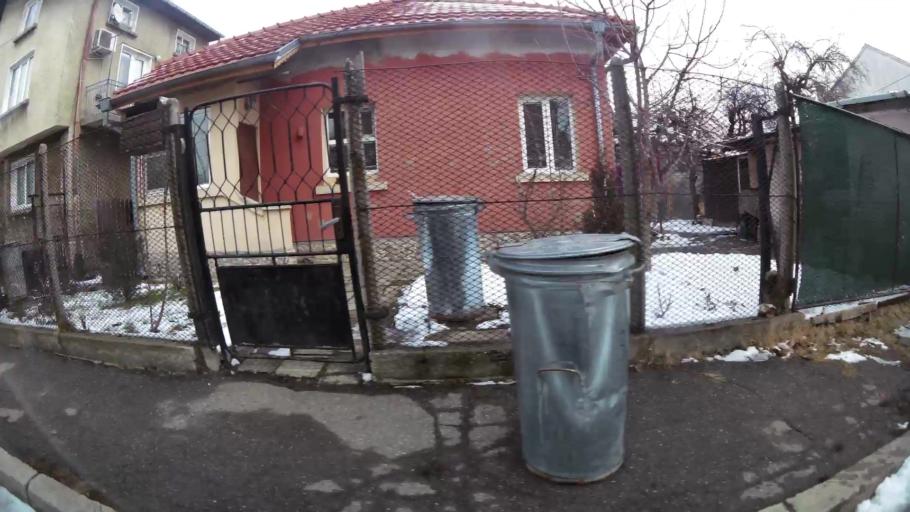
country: BG
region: Sofia-Capital
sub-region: Stolichna Obshtina
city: Sofia
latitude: 42.7051
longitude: 23.3734
